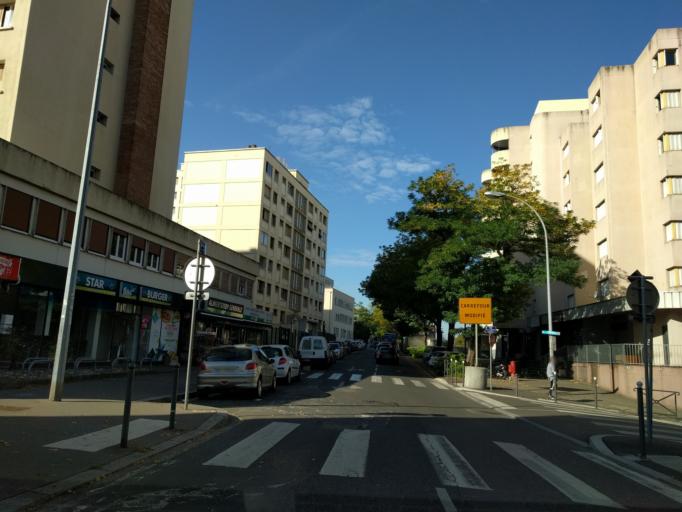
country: FR
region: Rhone-Alpes
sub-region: Departement du Rhone
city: Villeurbanne
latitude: 45.7619
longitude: 4.8980
